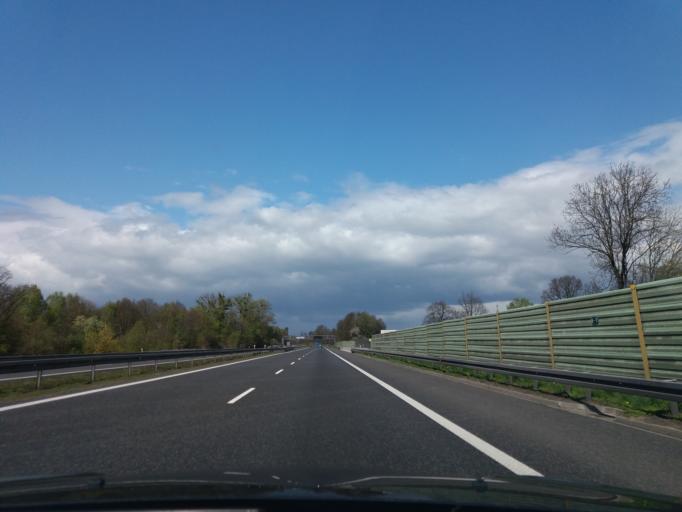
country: PL
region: Opole Voivodeship
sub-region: Powiat strzelecki
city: Ujazd
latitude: 50.4350
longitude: 18.3668
